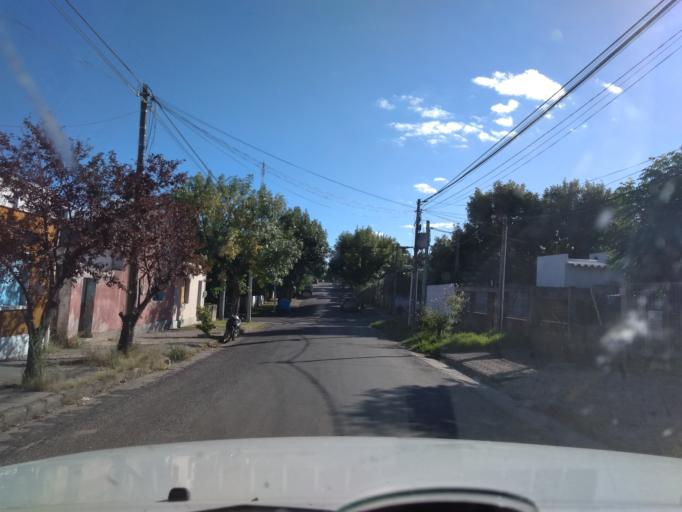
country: UY
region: Florida
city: Florida
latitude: -34.0948
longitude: -56.2100
